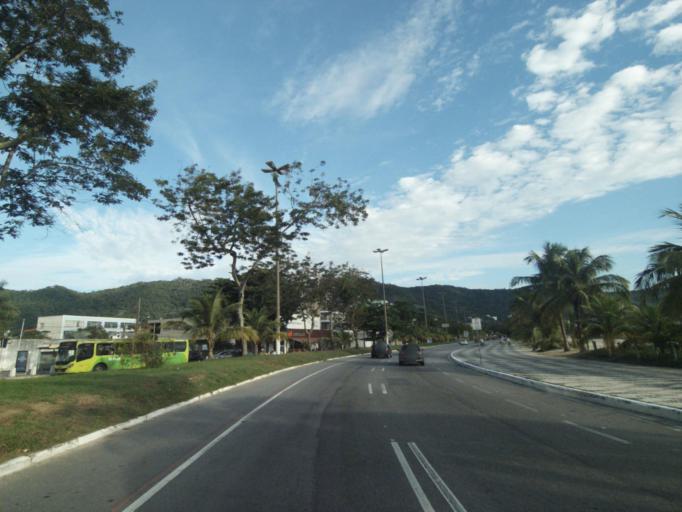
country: BR
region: Rio de Janeiro
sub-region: Niteroi
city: Niteroi
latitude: -22.9159
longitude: -43.0950
